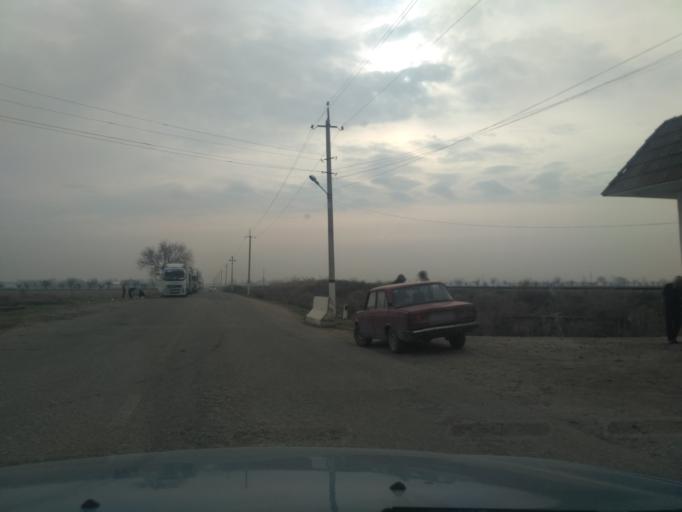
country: KZ
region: Ongtustik Qazaqstan
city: Ilyich
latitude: 40.8345
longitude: 68.5732
